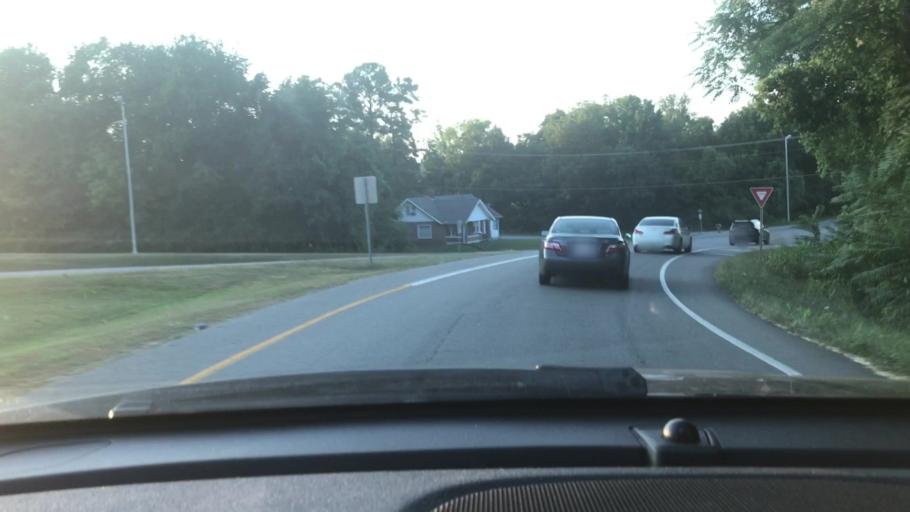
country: US
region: Tennessee
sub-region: Dickson County
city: Dickson
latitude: 36.0835
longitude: -87.3792
